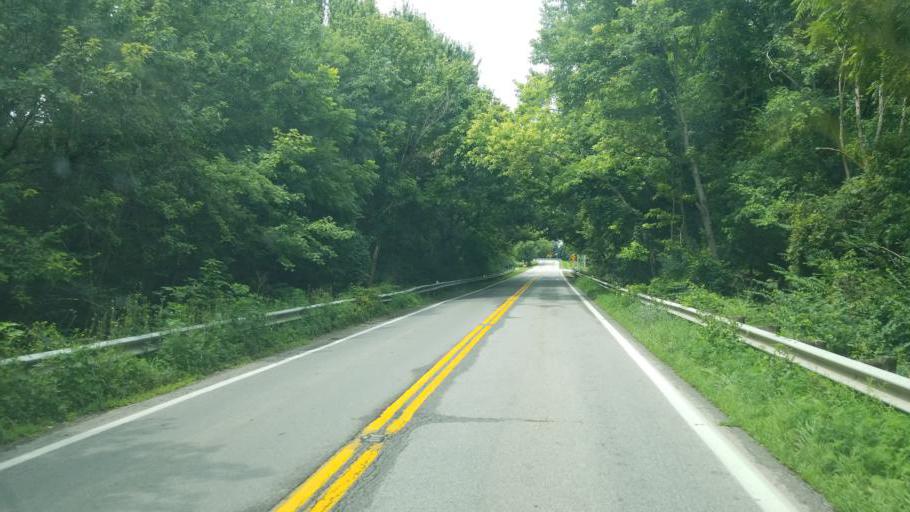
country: US
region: Ohio
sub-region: Pickaway County
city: Commercial Point
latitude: 39.8323
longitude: -83.0146
